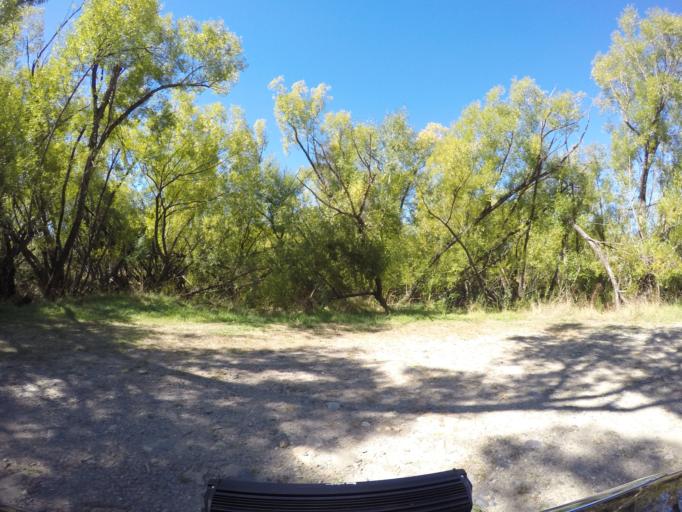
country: AU
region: New South Wales
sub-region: Snowy River
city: Jindabyne
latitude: -36.2167
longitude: 148.1075
